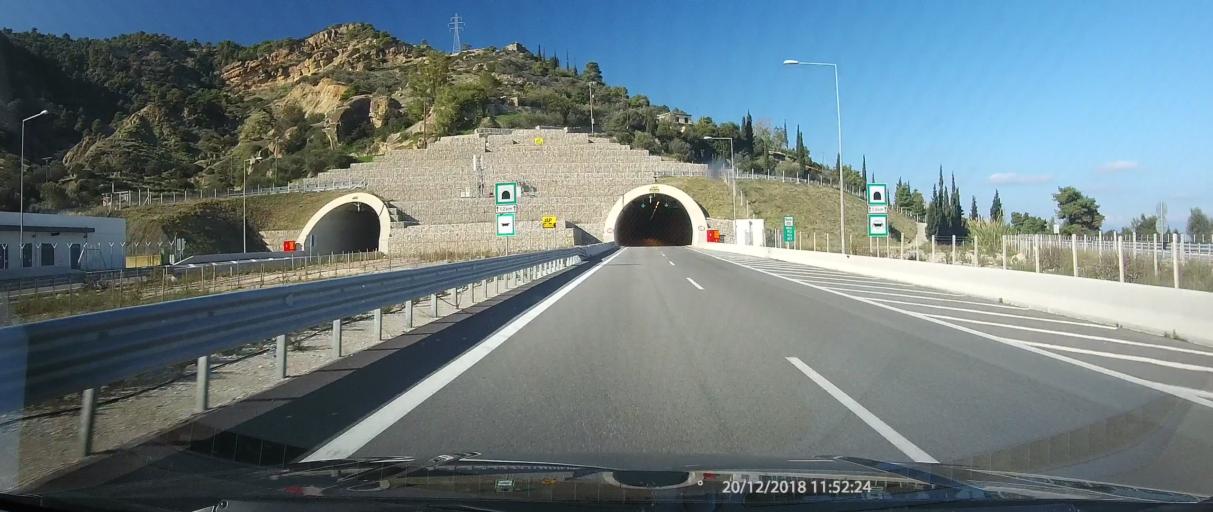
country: GR
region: West Greece
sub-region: Nomos Achaias
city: Aiyira
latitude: 38.1347
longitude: 22.3899
